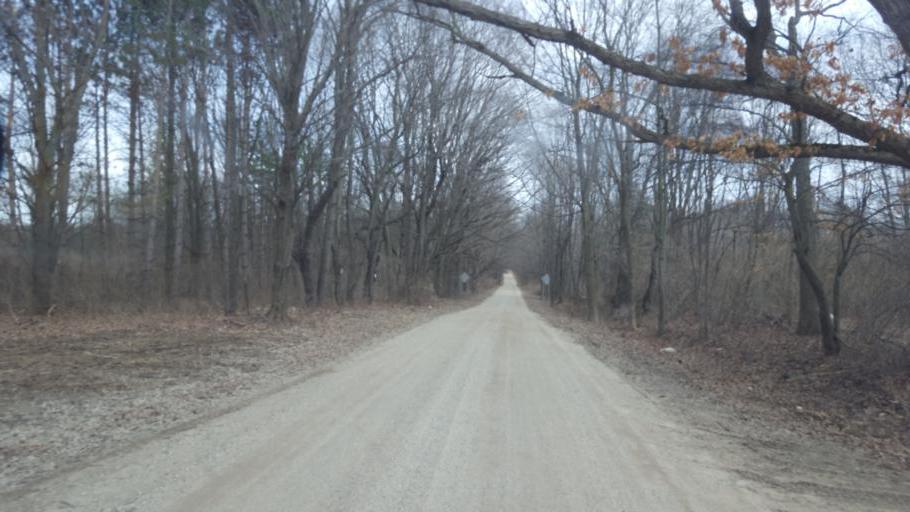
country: US
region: Michigan
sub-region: Isabella County
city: Lake Isabella
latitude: 43.6828
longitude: -85.1447
